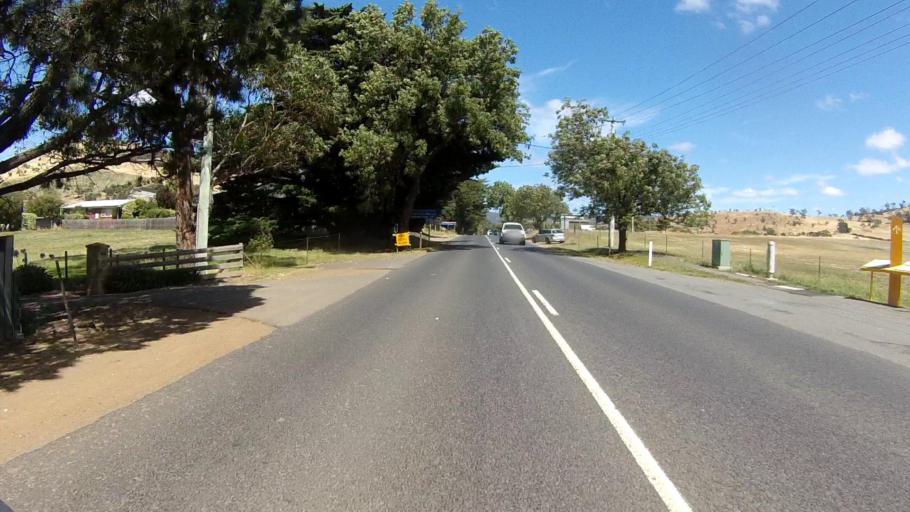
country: AU
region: Tasmania
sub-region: Clarence
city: Cambridge
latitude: -42.7377
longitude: 147.4323
